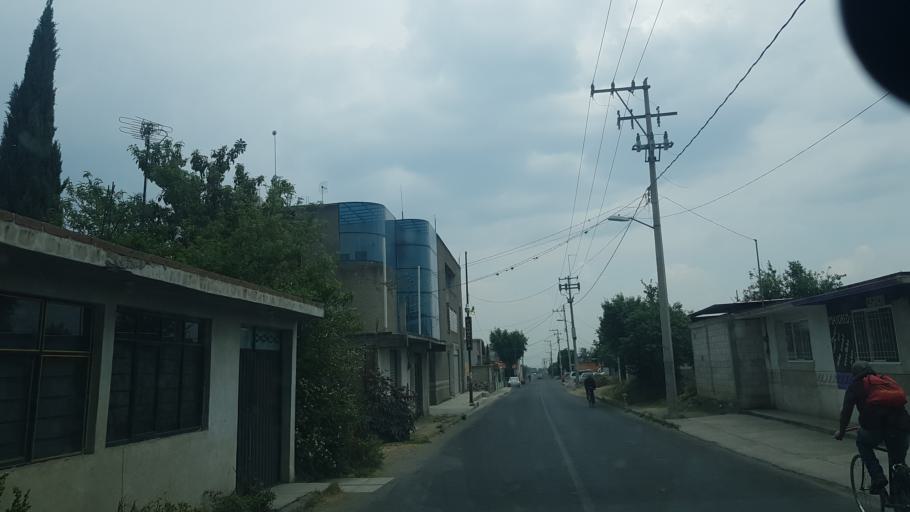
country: MX
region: Puebla
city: San Lorenzo Chiautzingo
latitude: 19.1998
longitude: -98.4586
